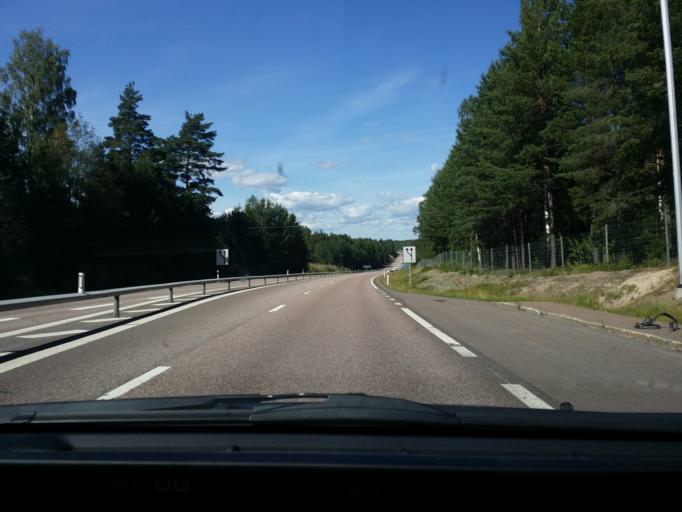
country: SE
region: Dalarna
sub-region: Hedemora Kommun
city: Brunna
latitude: 60.2310
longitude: 16.0354
